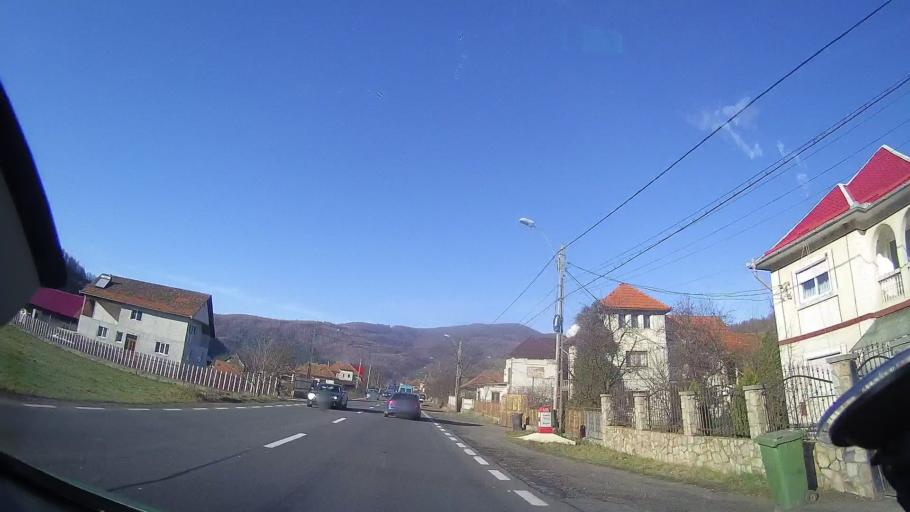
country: RO
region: Cluj
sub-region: Comuna Negreni
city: Negreni
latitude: 46.9584
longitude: 22.7439
